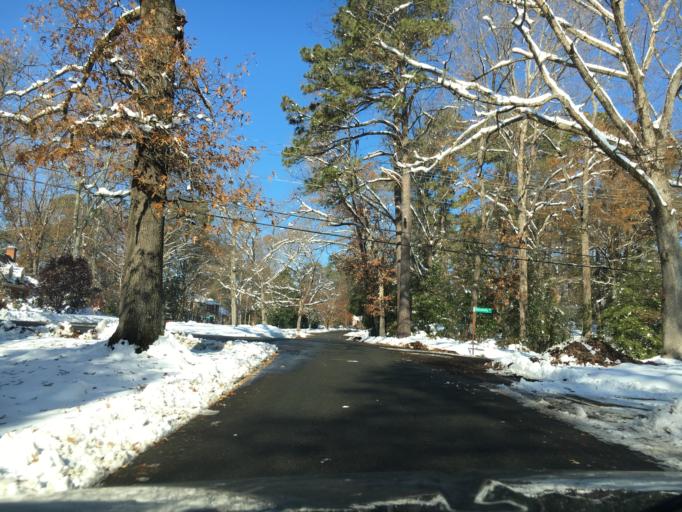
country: US
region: Virginia
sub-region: Henrico County
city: Tuckahoe
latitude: 37.5777
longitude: -77.5496
